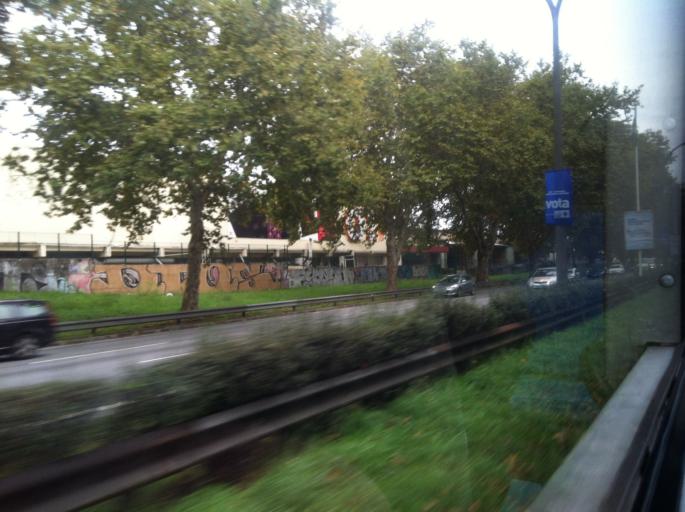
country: PT
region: Porto
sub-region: Matosinhos
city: Senhora da Hora
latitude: 41.1744
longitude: -8.6511
